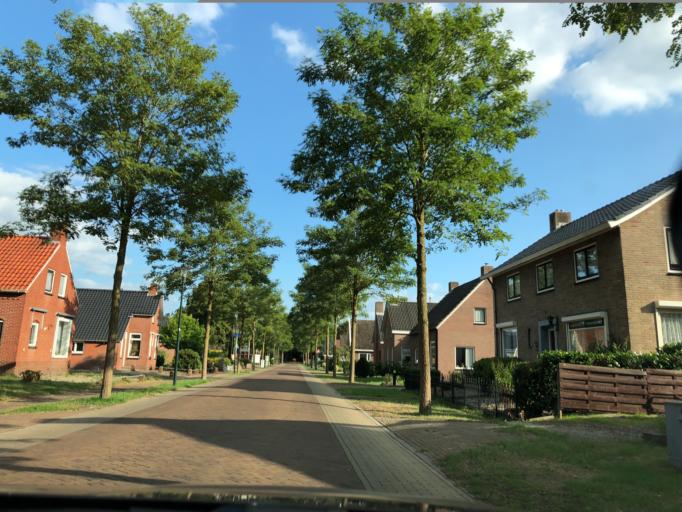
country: NL
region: Groningen
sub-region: Gemeente Vlagtwedde
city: Sellingen
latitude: 53.0099
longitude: 7.1859
